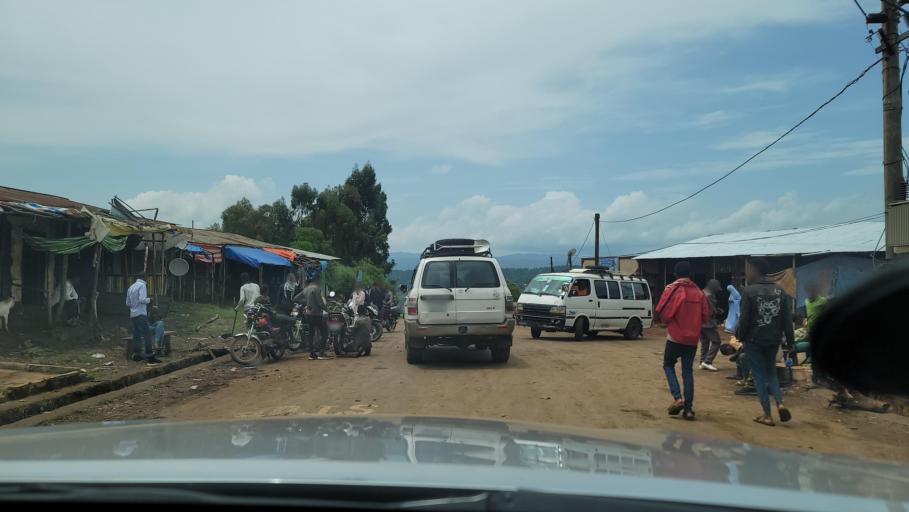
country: ET
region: Oromiya
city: Agaro
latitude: 7.7415
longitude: 36.2497
